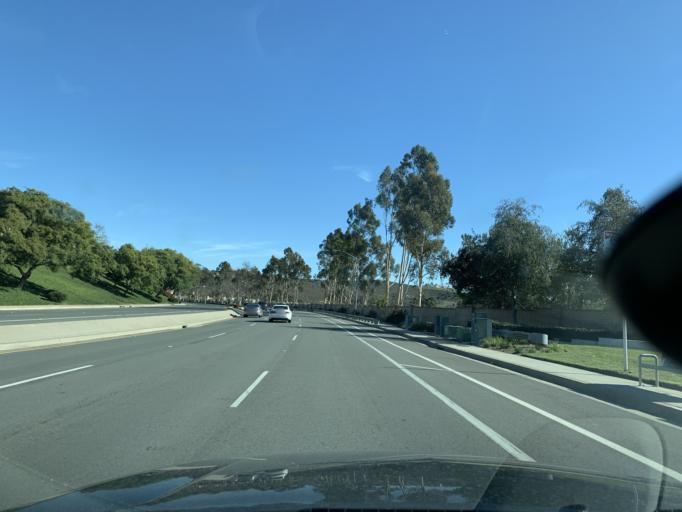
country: US
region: California
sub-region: San Diego County
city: Poway
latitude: 32.9456
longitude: -117.0839
